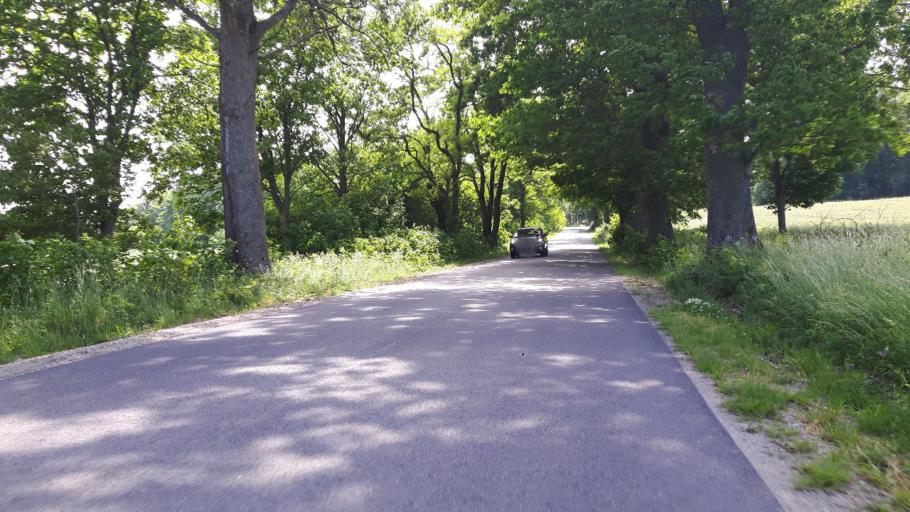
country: PL
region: Pomeranian Voivodeship
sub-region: Powiat wejherowski
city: Choczewo
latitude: 54.7497
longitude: 17.7944
